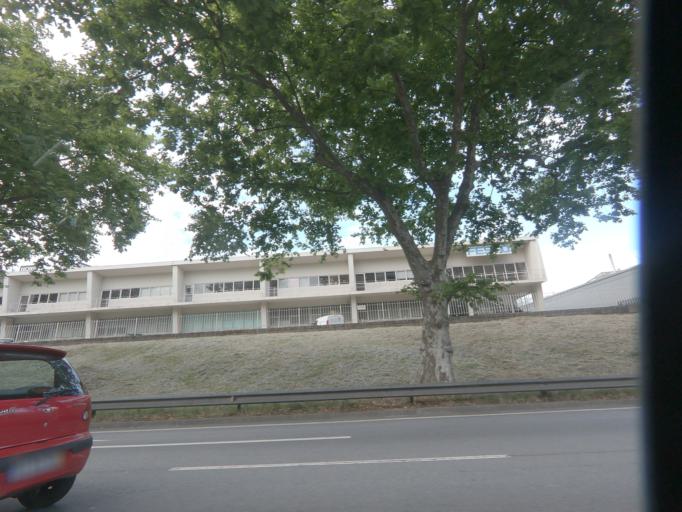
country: PT
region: Porto
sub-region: Matosinhos
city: Senhora da Hora
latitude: 41.1737
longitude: -8.6500
